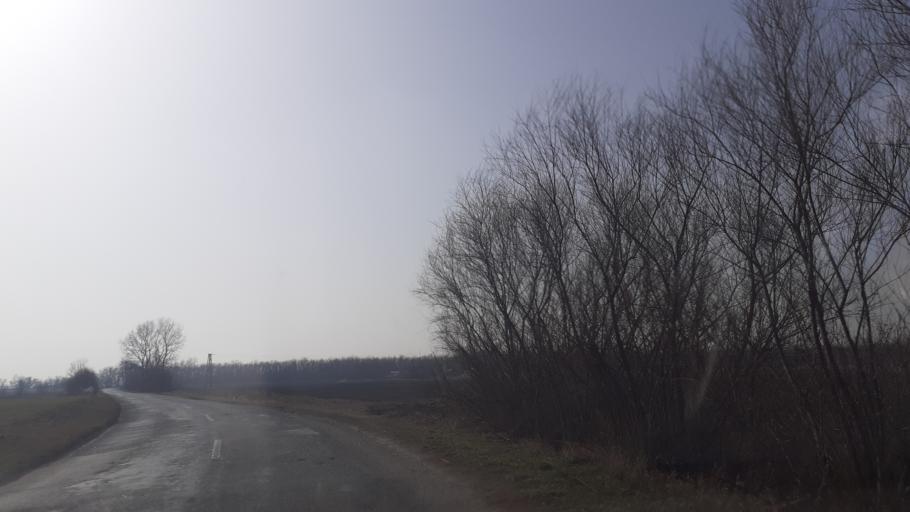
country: HU
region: Bacs-Kiskun
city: Kunszentmiklos
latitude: 47.0492
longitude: 19.2298
